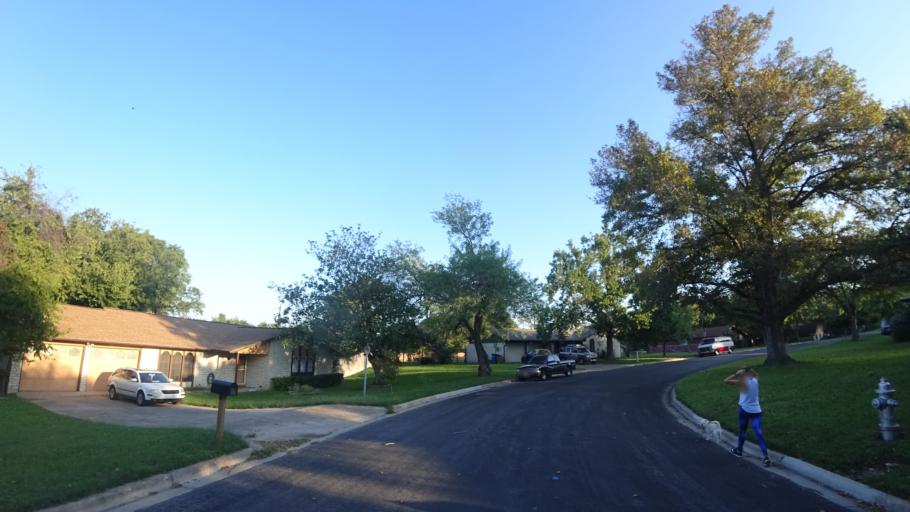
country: US
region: Texas
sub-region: Travis County
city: Wells Branch
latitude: 30.3685
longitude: -97.6745
